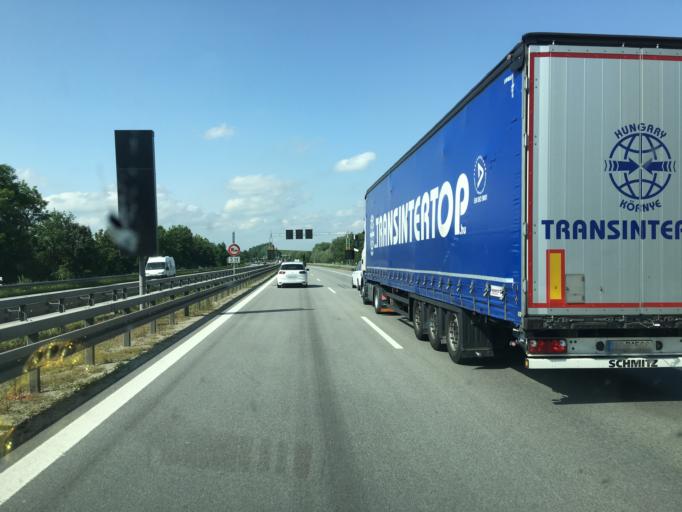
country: AT
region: Upper Austria
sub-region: Politischer Bezirk Scharding
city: Scharding
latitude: 48.4493
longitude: 13.3760
